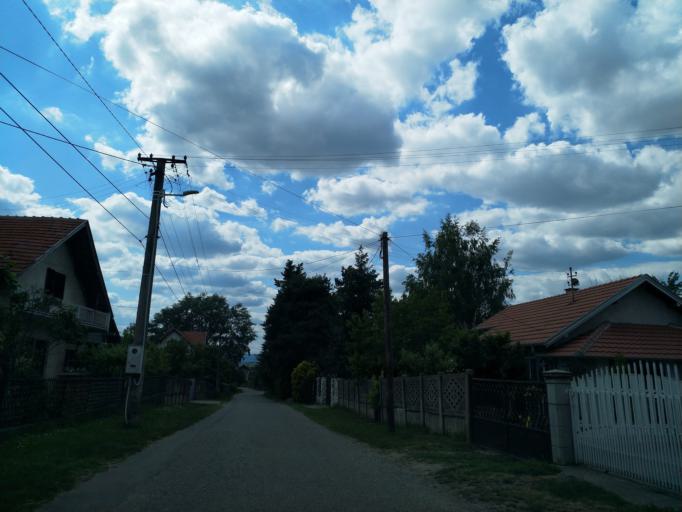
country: RS
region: Central Serbia
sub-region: Pomoravski Okrug
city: Cuprija
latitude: 43.9393
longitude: 21.3116
